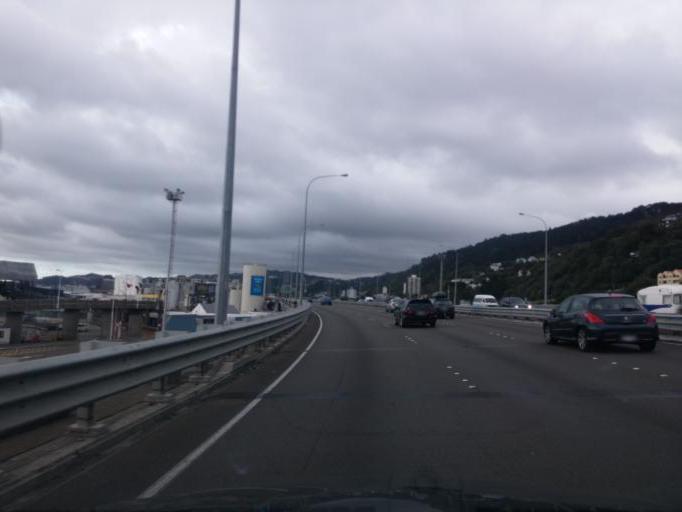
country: NZ
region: Wellington
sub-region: Wellington City
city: Wellington
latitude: -41.2627
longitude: 174.7882
